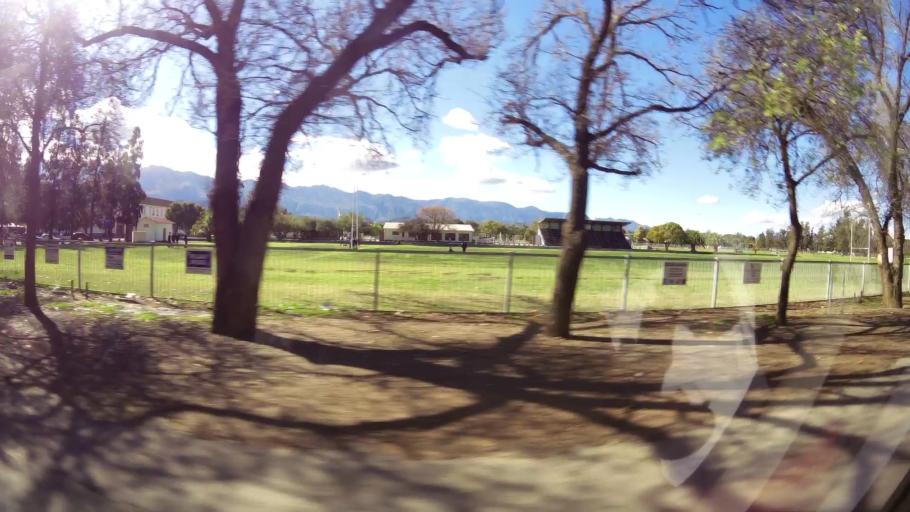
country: ZA
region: Western Cape
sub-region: Cape Winelands District Municipality
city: Ashton
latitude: -33.8089
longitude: 19.8875
